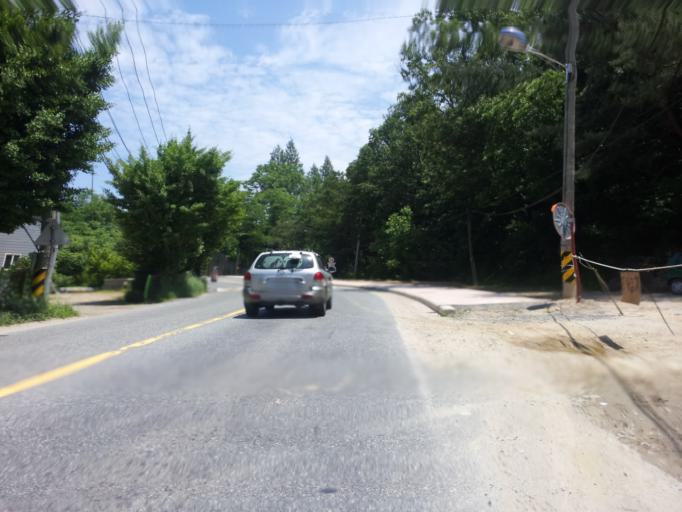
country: KR
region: Chungcheongbuk-do
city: Okcheon
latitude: 36.3098
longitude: 127.5620
